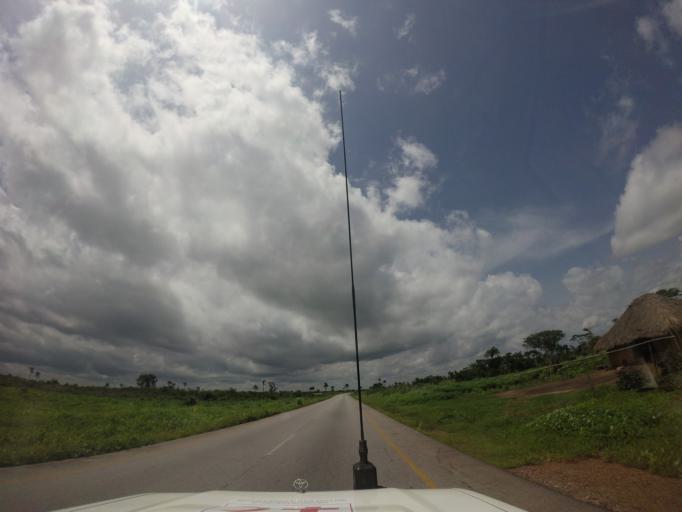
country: SL
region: Northern Province
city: Lunsar
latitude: 8.4724
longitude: -12.5597
